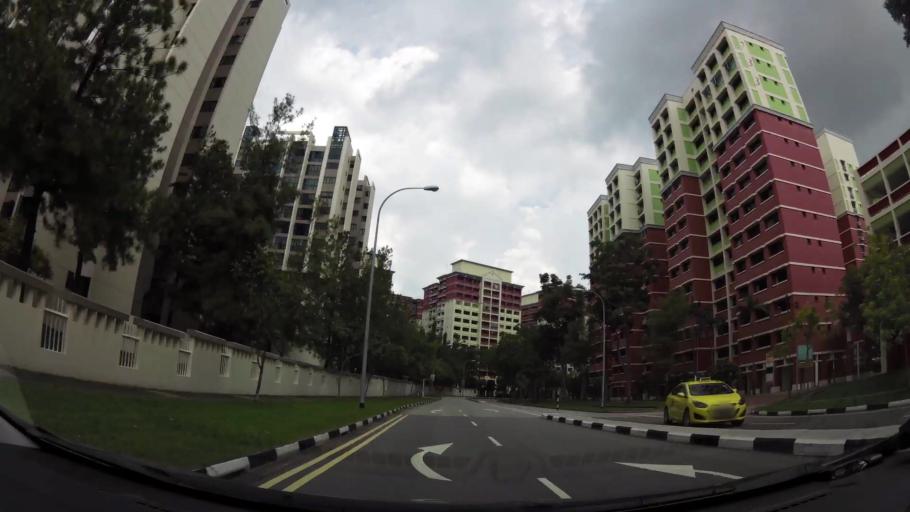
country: SG
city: Singapore
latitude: 1.3577
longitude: 103.9332
